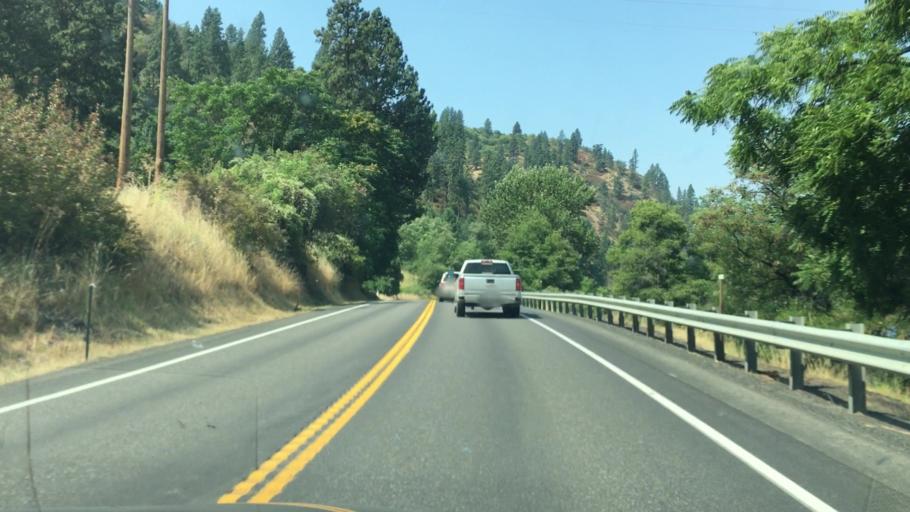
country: US
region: Idaho
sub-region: Clearwater County
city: Orofino
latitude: 46.4994
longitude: -116.4825
